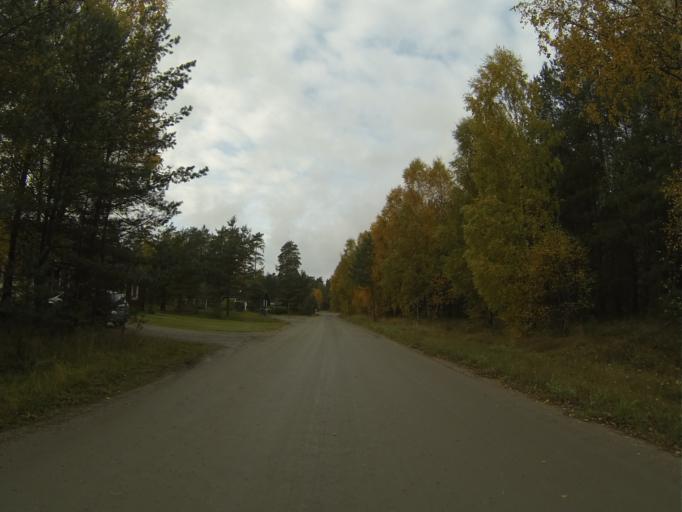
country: SE
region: Skane
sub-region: Sjobo Kommun
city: Blentarp
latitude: 55.6353
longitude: 13.6397
